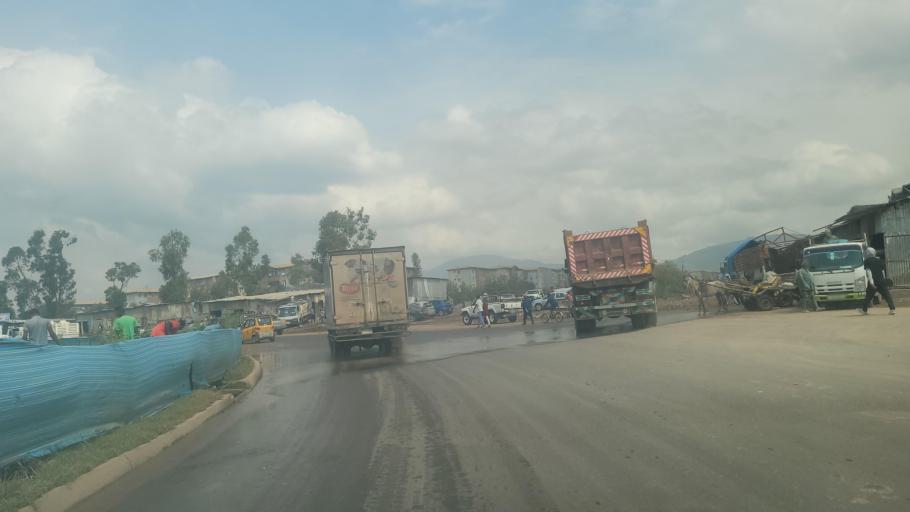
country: ET
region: Adis Abeba
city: Addis Ababa
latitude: 8.9551
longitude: 38.6971
